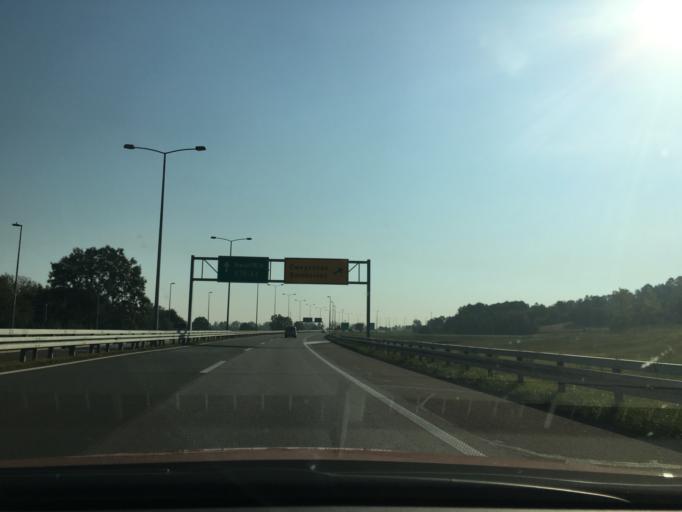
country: RS
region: Central Serbia
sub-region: Podunavski Okrug
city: Smederevo
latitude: 44.5842
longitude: 20.9631
